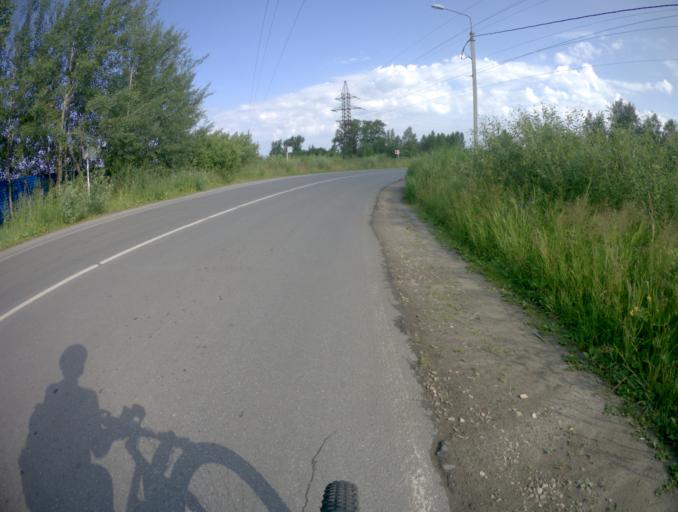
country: RU
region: Vladimir
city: Novovyazniki
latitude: 56.2068
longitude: 42.1633
